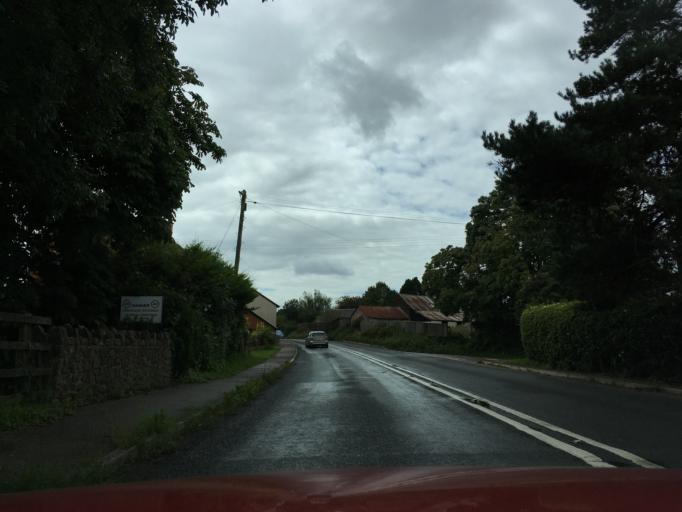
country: GB
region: England
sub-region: Devon
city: Cullompton
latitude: 50.8771
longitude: -3.3859
